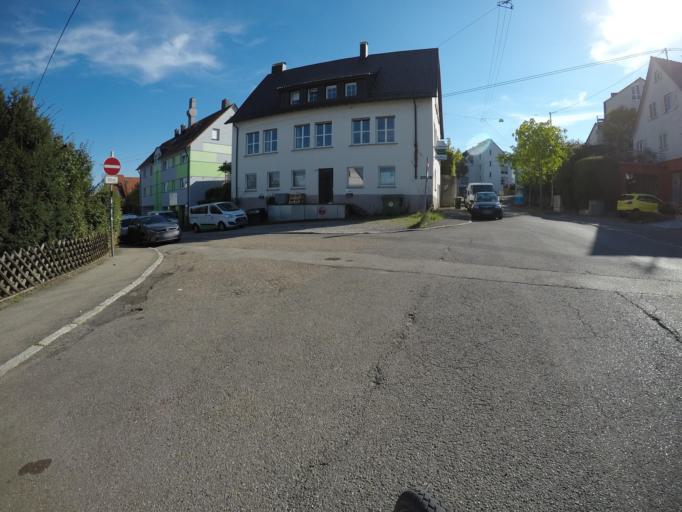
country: DE
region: Baden-Wuerttemberg
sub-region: Regierungsbezirk Stuttgart
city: Steinenbronn
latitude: 48.7189
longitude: 9.1022
